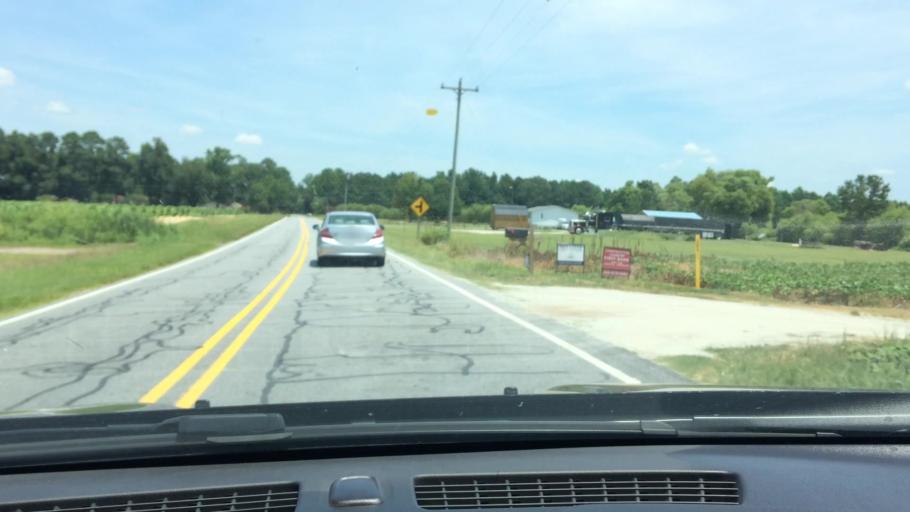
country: US
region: North Carolina
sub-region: Beaufort County
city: Washington
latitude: 35.5927
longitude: -77.1620
